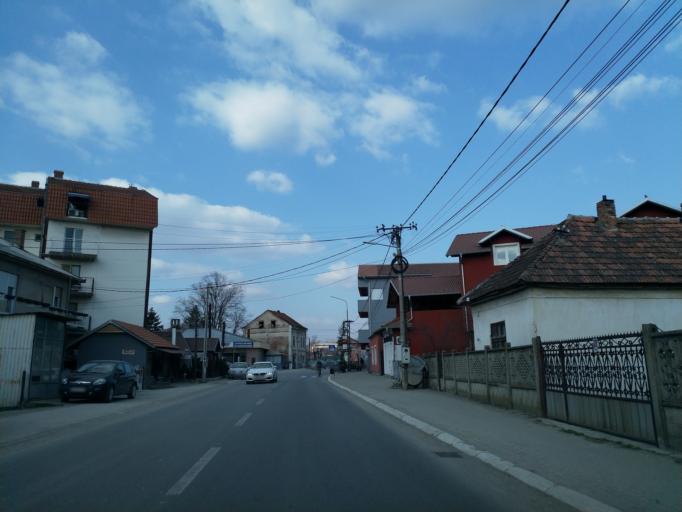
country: RS
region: Central Serbia
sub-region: Sumadijski Okrug
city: Batocina
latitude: 44.1498
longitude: 21.0776
